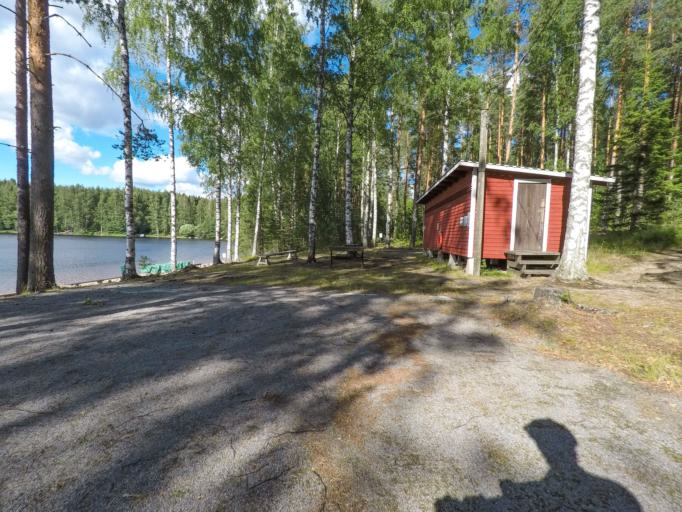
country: FI
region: South Karelia
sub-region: Lappeenranta
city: Joutseno
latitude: 61.1533
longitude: 28.5671
